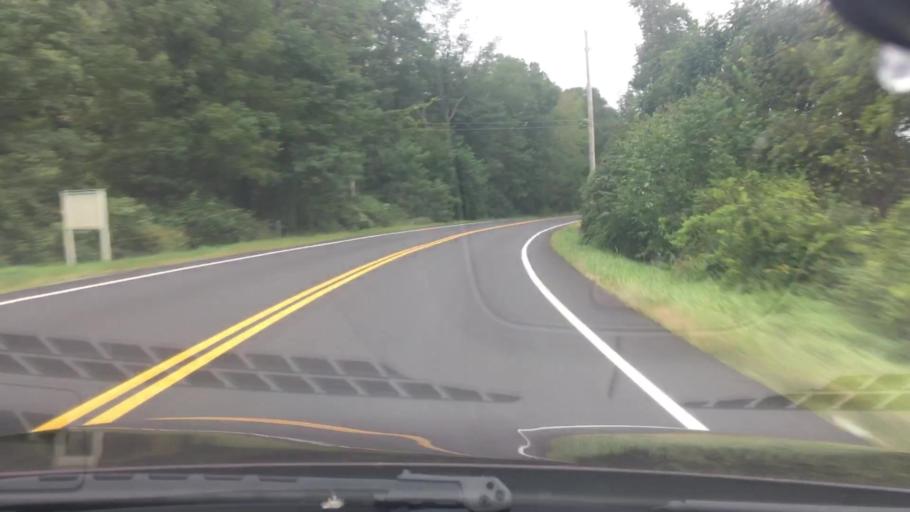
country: US
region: New York
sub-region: Dutchess County
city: Dover Plains
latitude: 41.8437
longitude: -73.5953
